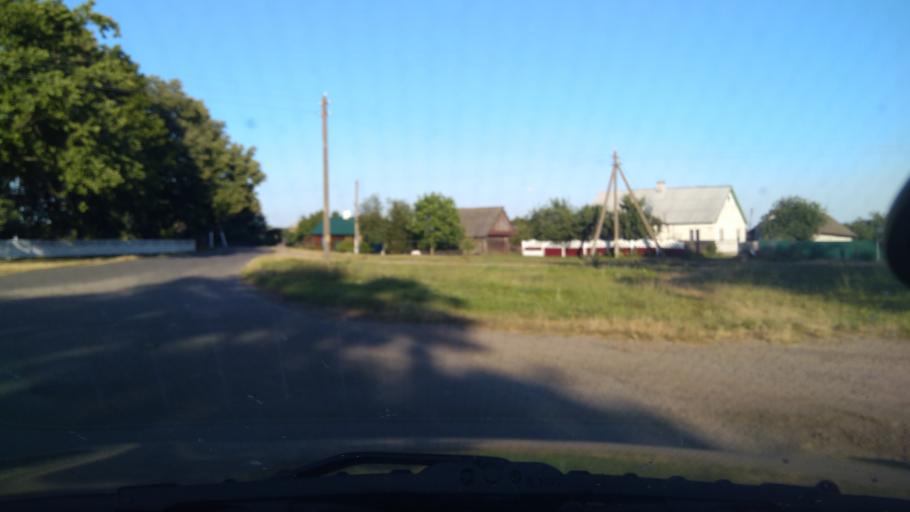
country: BY
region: Brest
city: Byaroza
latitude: 52.5886
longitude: 24.8713
